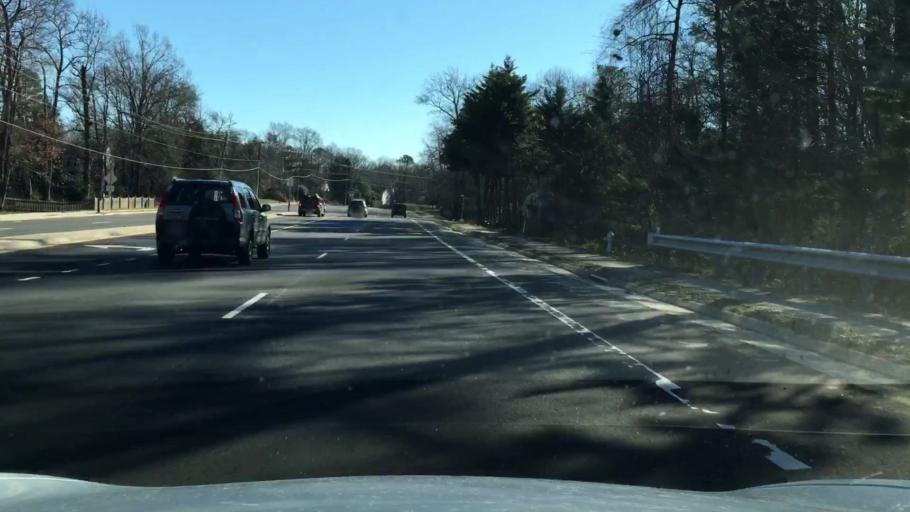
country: US
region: Virginia
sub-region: Chesterfield County
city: Bon Air
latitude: 37.5165
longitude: -77.5957
